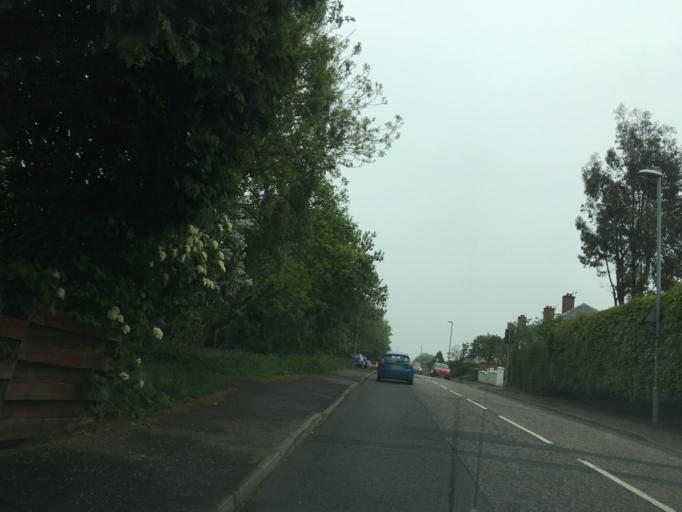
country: GB
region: Scotland
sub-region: Midlothian
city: Penicuik
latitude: 55.8463
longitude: -3.1925
